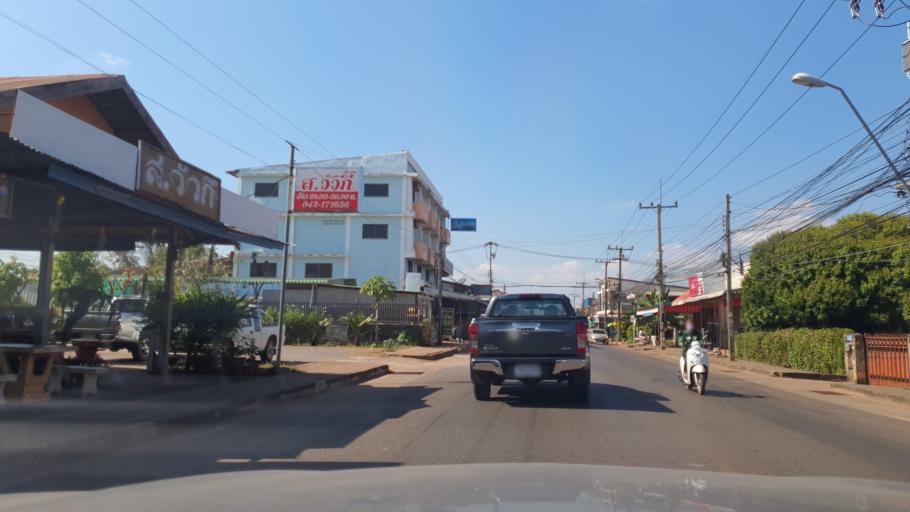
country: TH
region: Sakon Nakhon
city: Sakon Nakhon
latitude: 17.1627
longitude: 104.1258
